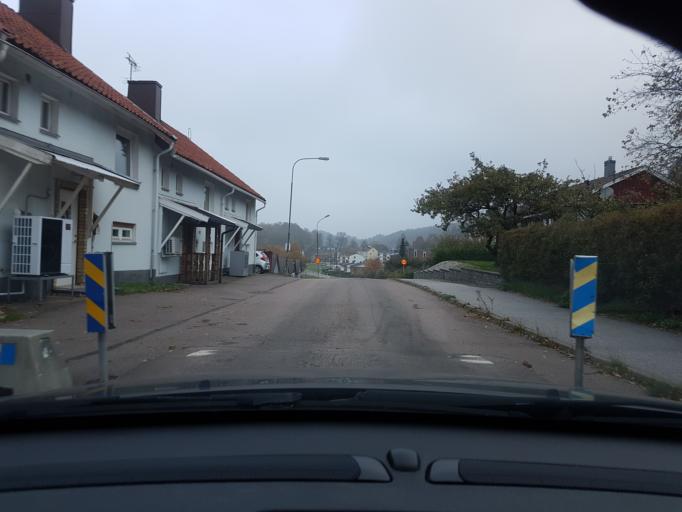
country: SE
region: Vaestra Goetaland
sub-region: Ale Kommun
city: Surte
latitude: 57.8268
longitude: 12.0209
